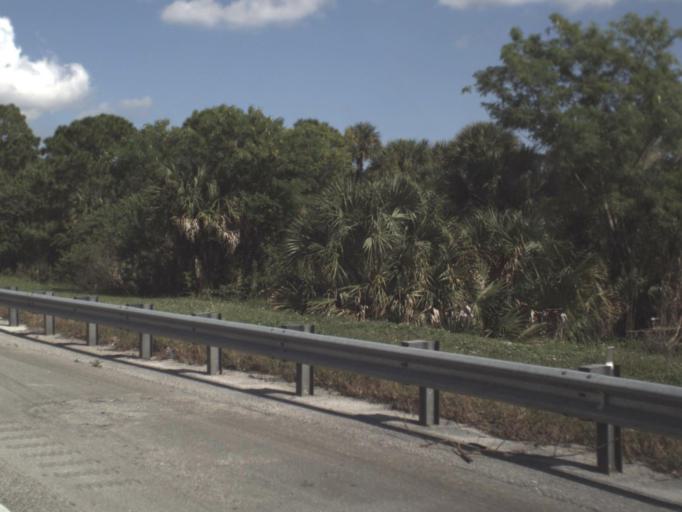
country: US
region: Florida
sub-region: Palm Beach County
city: Palm Beach Gardens
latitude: 26.7859
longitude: -80.1320
